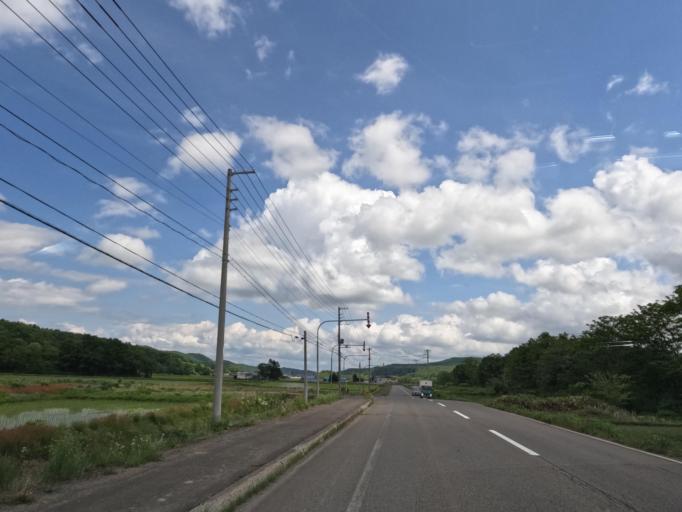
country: JP
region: Hokkaido
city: Takikawa
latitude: 43.5872
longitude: 141.7677
